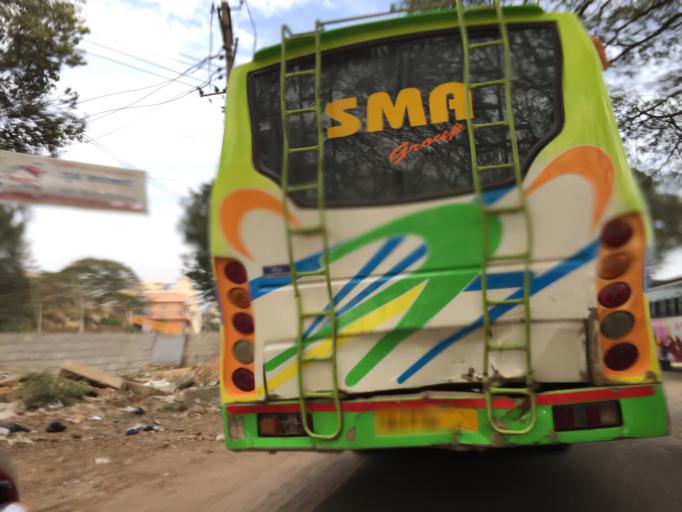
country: IN
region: Karnataka
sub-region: Kolar
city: Kolar
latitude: 13.1310
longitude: 78.1281
